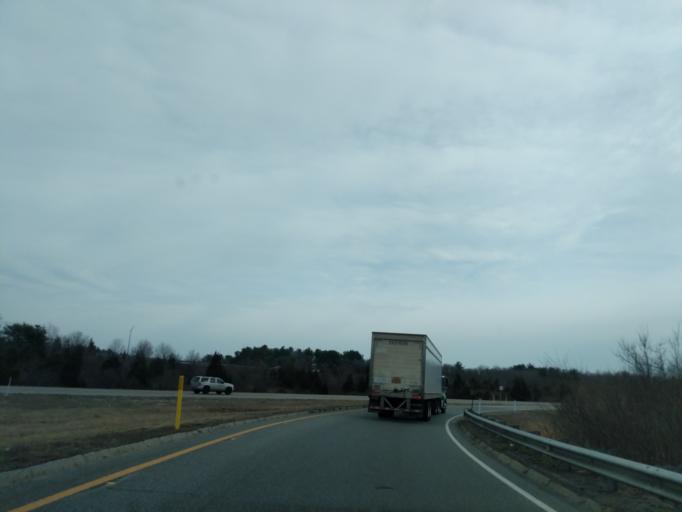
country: US
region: Massachusetts
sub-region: Bristol County
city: Raynham Center
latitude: 41.9449
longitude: -71.0229
